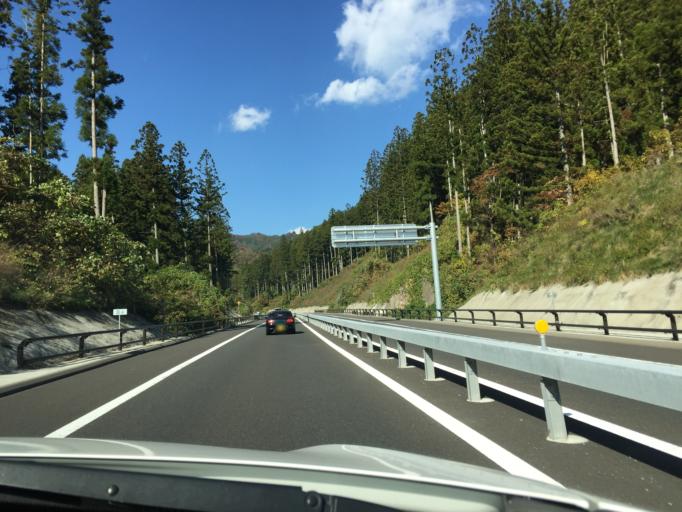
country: JP
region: Miyagi
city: Marumori
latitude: 37.7817
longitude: 140.8267
